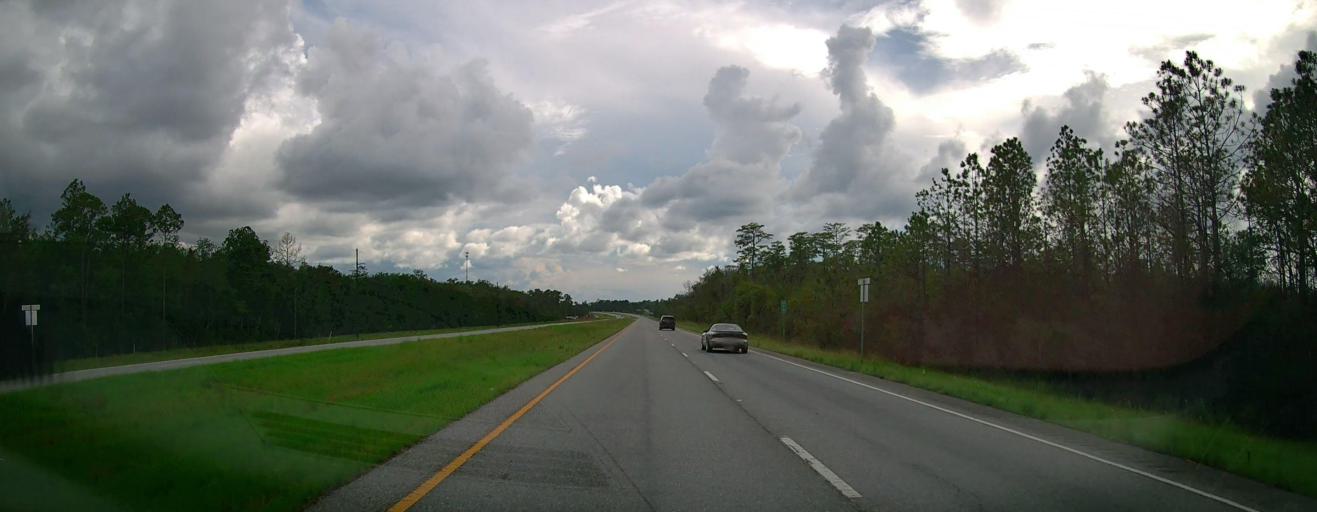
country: US
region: Georgia
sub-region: Pierce County
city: Blackshear
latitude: 31.4390
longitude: -82.0806
